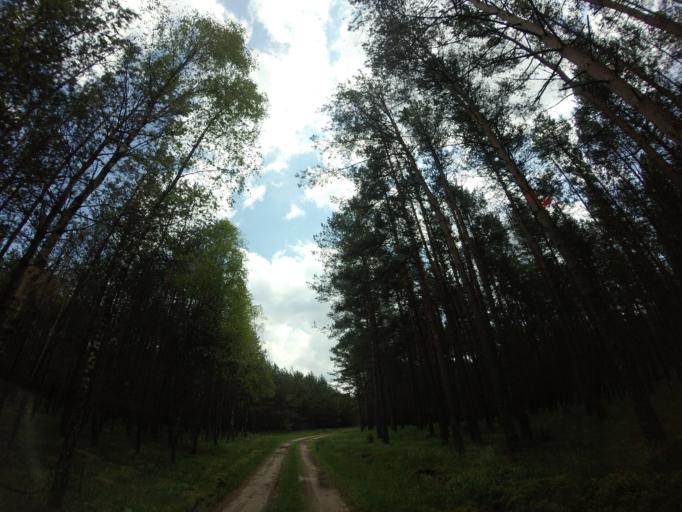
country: PL
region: West Pomeranian Voivodeship
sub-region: Powiat drawski
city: Kalisz Pomorski
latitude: 53.2204
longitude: 15.9435
